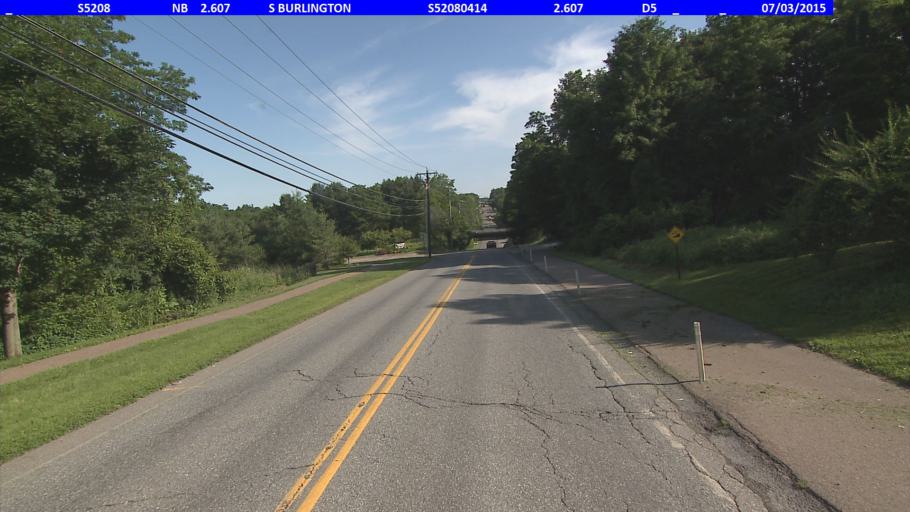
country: US
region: Vermont
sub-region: Chittenden County
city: South Burlington
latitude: 44.4479
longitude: -73.1778
